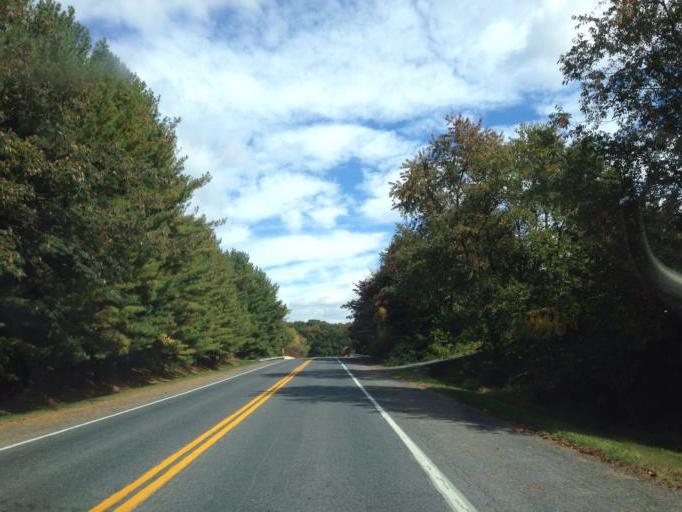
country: US
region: Maryland
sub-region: Carroll County
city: Mount Airy
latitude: 39.3517
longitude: -77.1226
